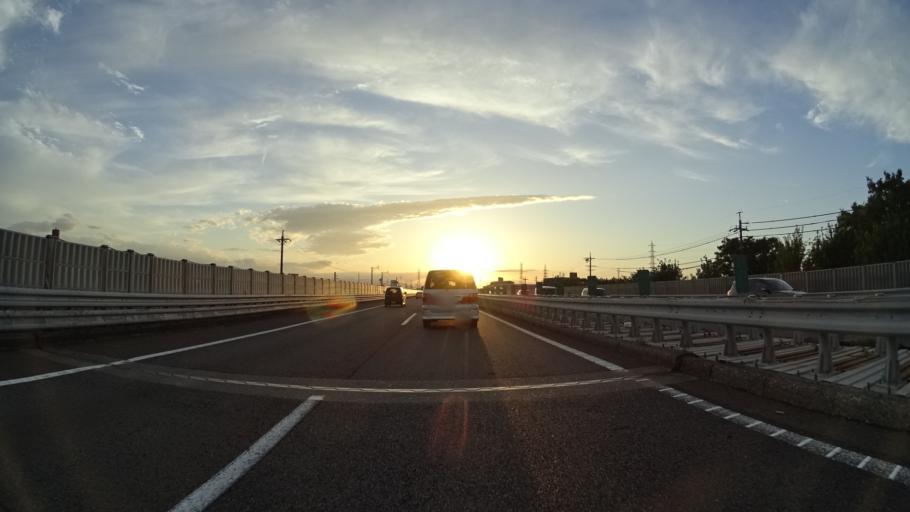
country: JP
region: Aichi
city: Ichinomiya
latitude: 35.2759
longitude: 136.8161
